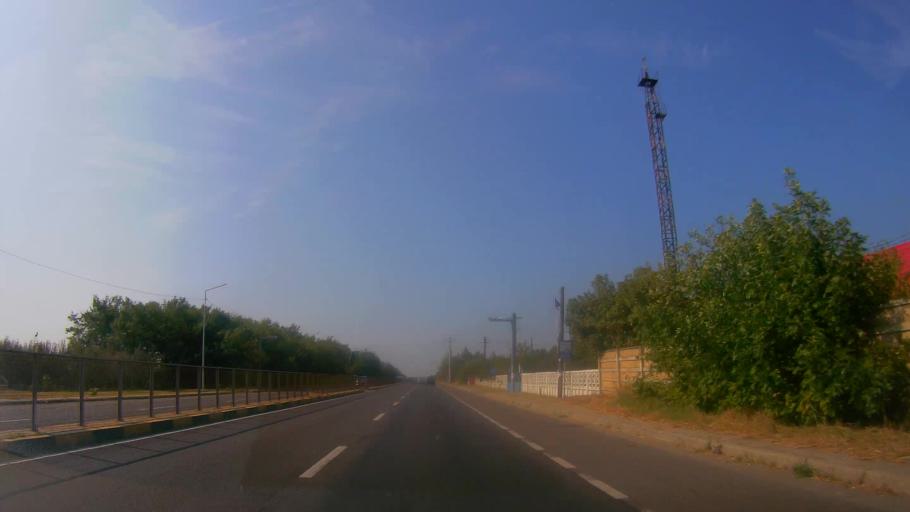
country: RO
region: Giurgiu
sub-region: Comuna Calugareni
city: Calugareni
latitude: 44.1981
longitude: 26.0104
